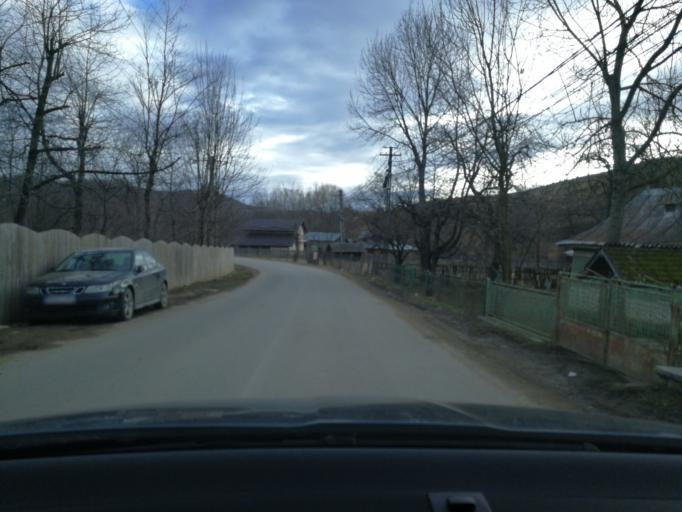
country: RO
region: Prahova
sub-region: Oras Breaza
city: Valea Tarsei
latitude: 45.1835
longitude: 25.6314
